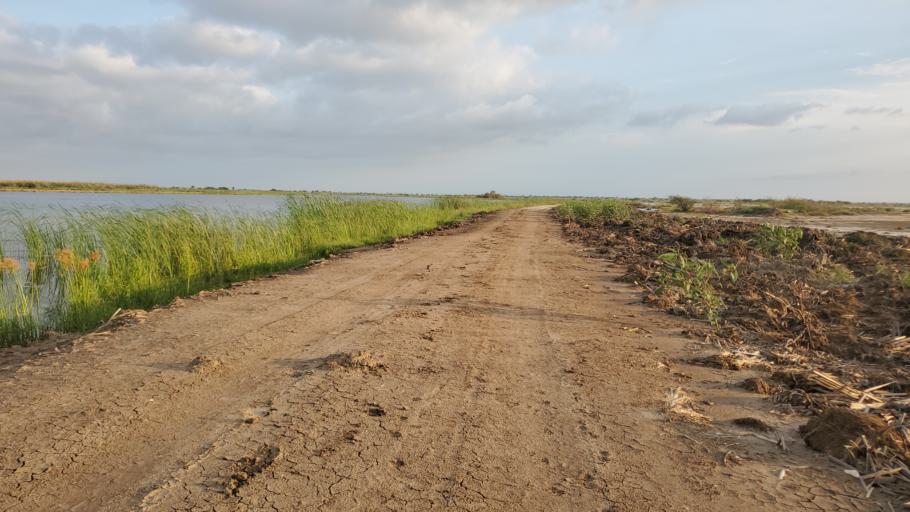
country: SN
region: Saint-Louis
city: Saint-Louis
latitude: 16.0290
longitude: -16.4104
